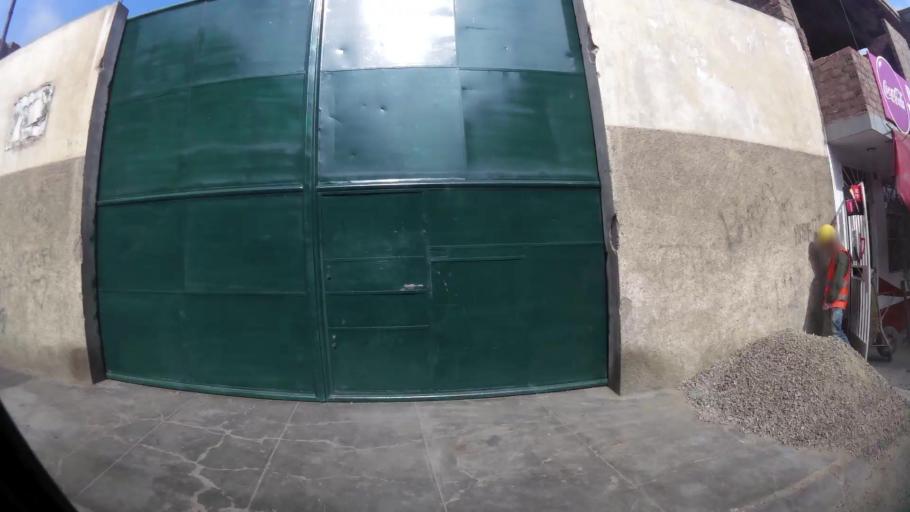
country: PE
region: La Libertad
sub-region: Provincia de Trujillo
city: Trujillo
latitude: -8.1070
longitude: -79.0170
